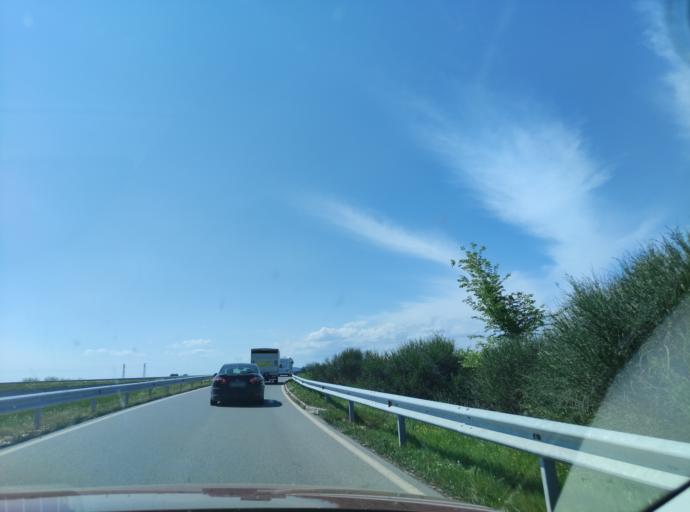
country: BG
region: Stara Zagora
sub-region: Obshtina Stara Zagora
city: Stara Zagora
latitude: 42.3407
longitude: 25.6641
